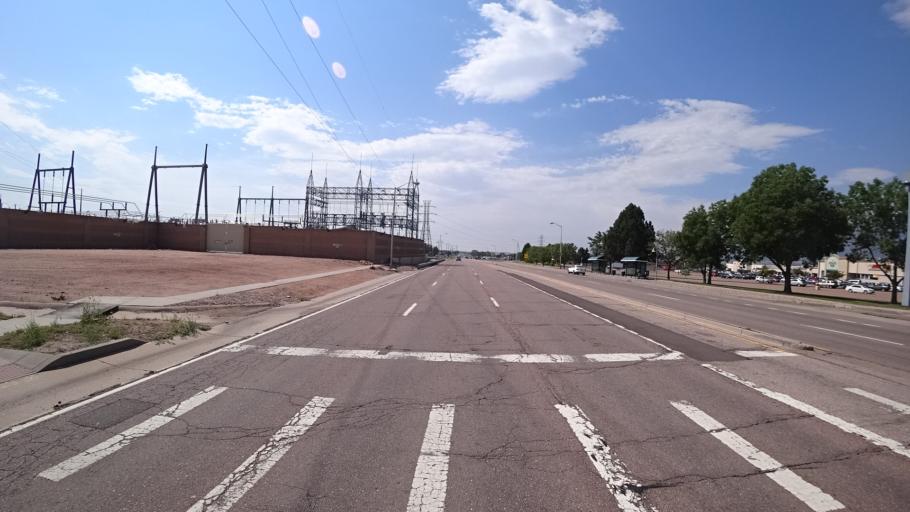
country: US
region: Colorado
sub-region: El Paso County
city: Stratmoor
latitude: 38.7928
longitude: -104.7575
